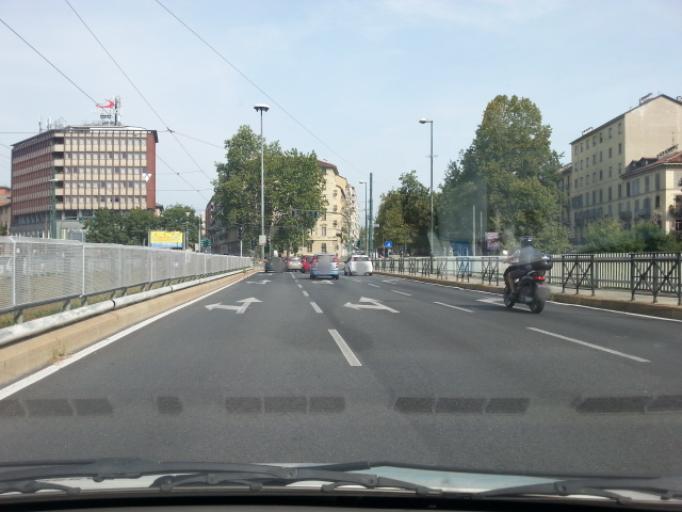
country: IT
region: Piedmont
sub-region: Provincia di Torino
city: Turin
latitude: 45.0683
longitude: 7.7084
